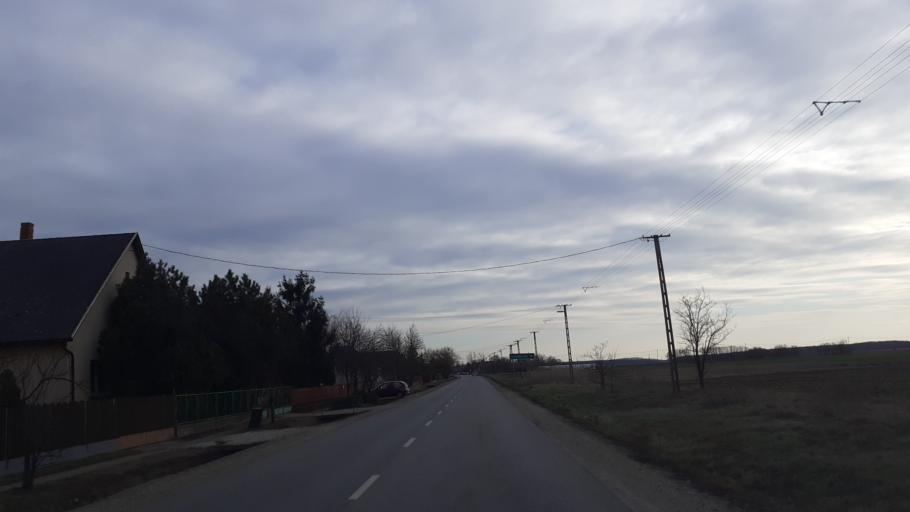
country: HU
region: Fejer
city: Sarbogard
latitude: 46.9431
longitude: 18.5932
